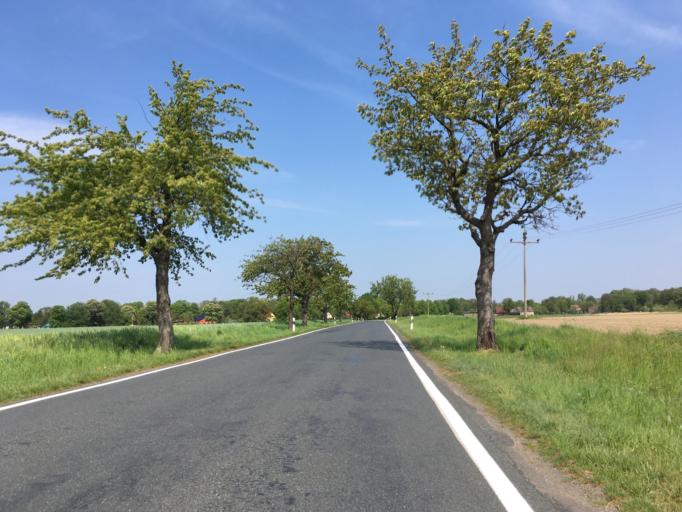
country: DE
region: Brandenburg
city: Melchow
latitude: 52.7311
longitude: 13.7102
